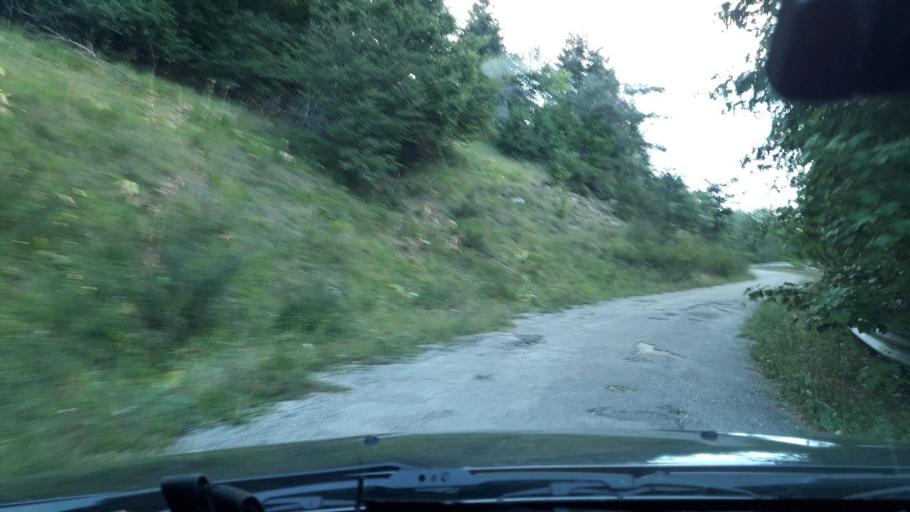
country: FR
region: Rhone-Alpes
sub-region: Departement de l'Isere
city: Mens
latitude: 44.7240
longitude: 5.6719
